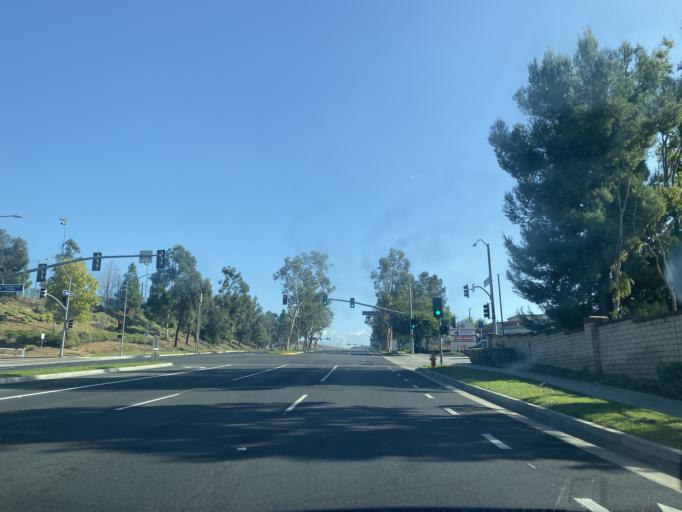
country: US
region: California
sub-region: Orange County
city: North Tustin
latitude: 33.7931
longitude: -117.7646
